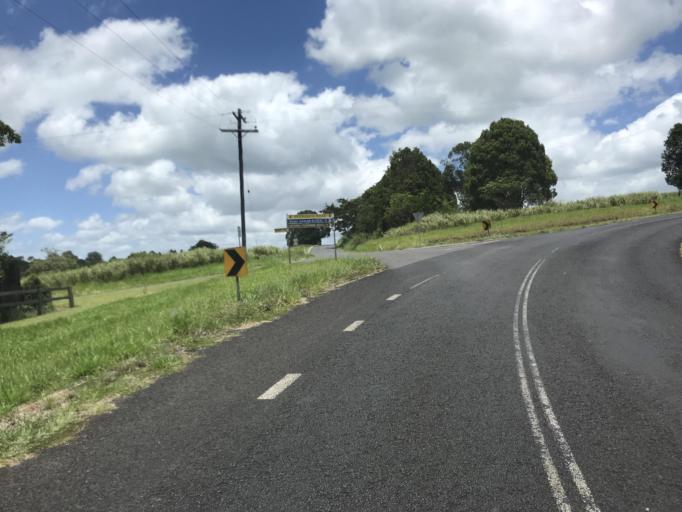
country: AU
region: Queensland
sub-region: Tablelands
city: Atherton
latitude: -17.3403
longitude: 145.5880
